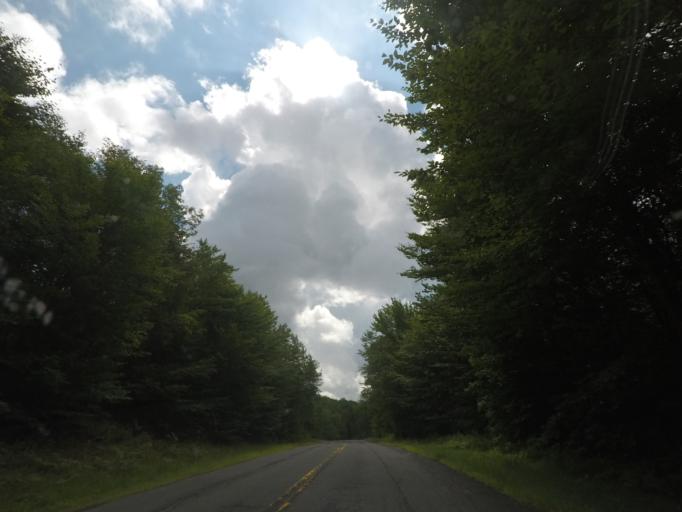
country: US
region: New York
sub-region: Rensselaer County
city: Averill Park
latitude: 42.6747
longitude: -73.4229
